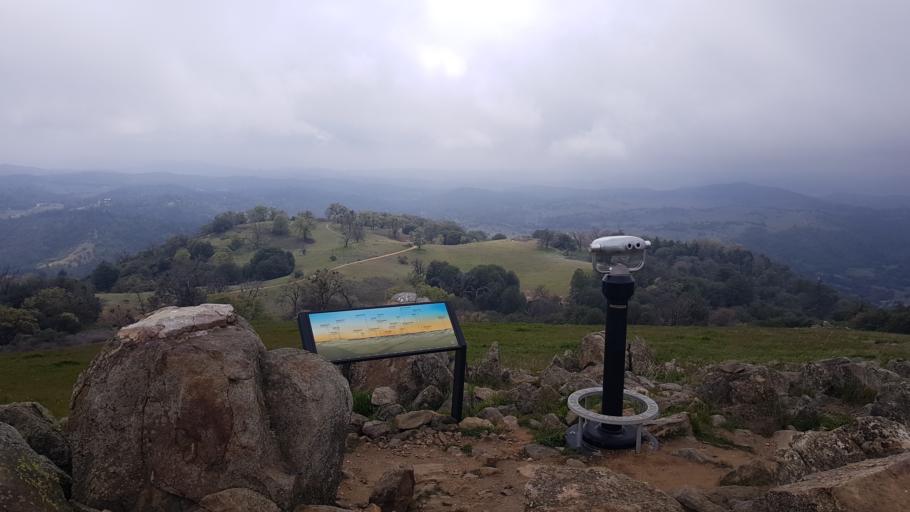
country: US
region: California
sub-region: San Diego County
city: Julian
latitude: 33.1054
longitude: -116.5826
